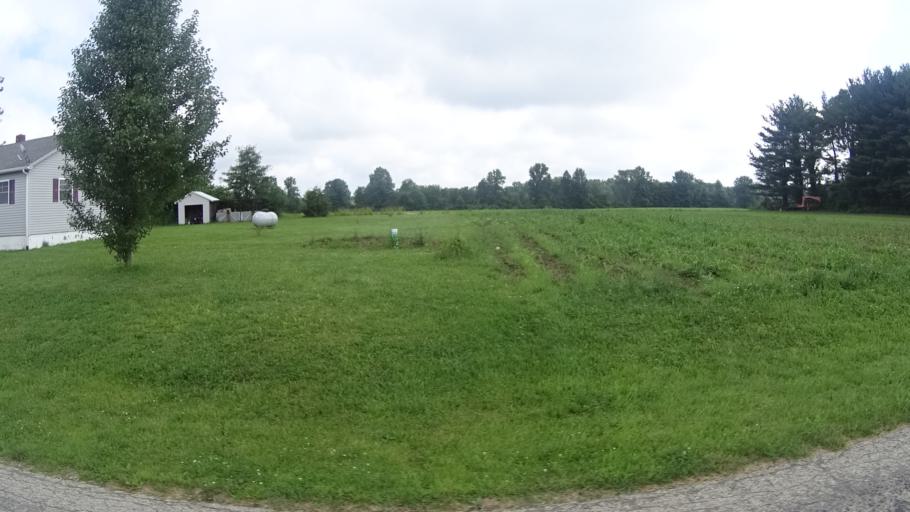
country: US
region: Ohio
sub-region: Huron County
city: Wakeman
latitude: 41.3089
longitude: -82.4353
